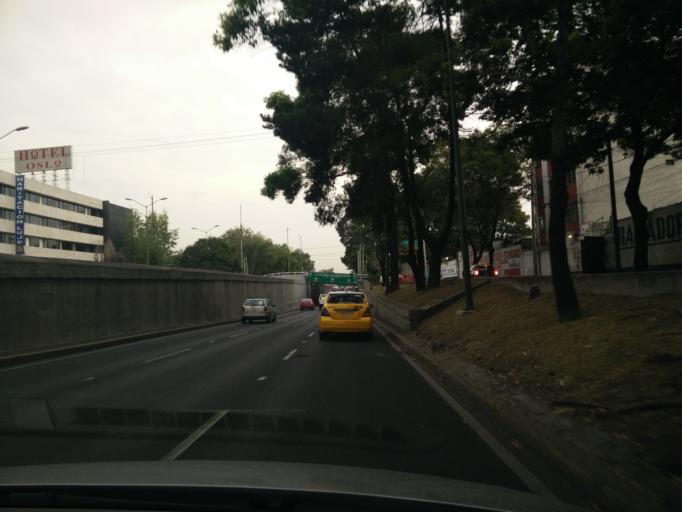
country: MX
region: Mexico City
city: Benito Juarez
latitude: 19.4038
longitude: -99.1462
